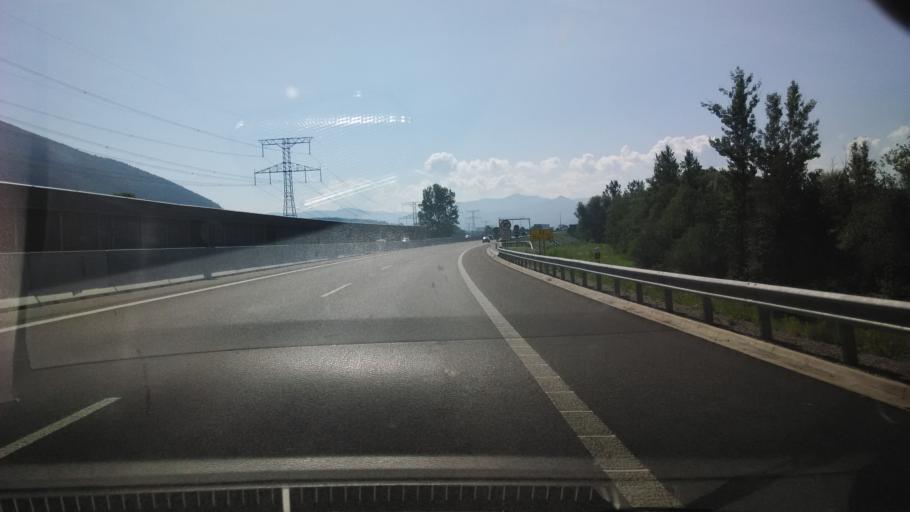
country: SK
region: Zilinsky
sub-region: Okres Zilina
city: Vrutky
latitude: 49.1308
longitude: 18.9063
